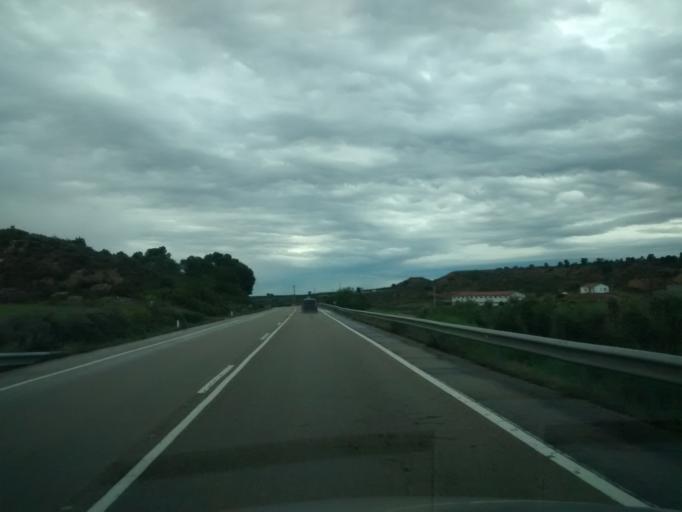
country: ES
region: Aragon
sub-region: Provincia de Zaragoza
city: Maella
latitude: 41.1709
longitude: 0.0707
